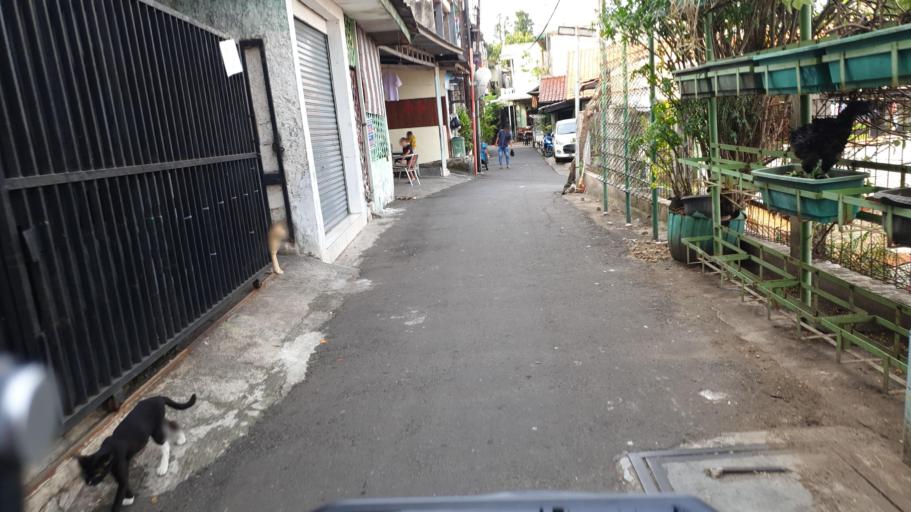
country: ID
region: Banten
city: South Tangerang
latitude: -6.2758
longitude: 106.7922
